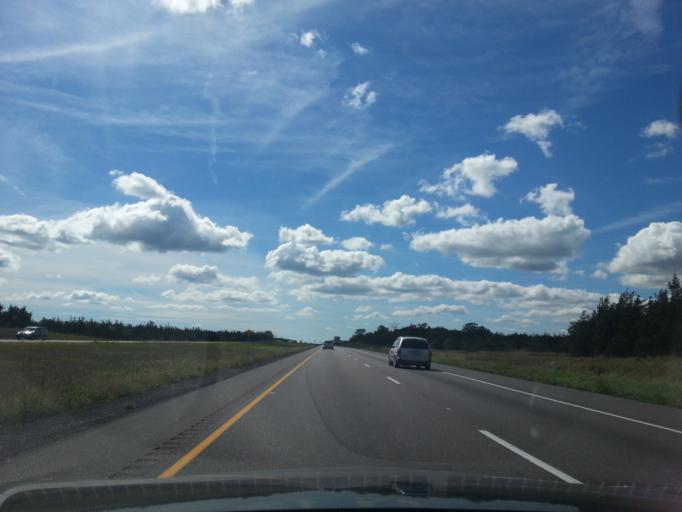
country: CA
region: Ontario
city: Deseronto
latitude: 44.2492
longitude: -77.0299
